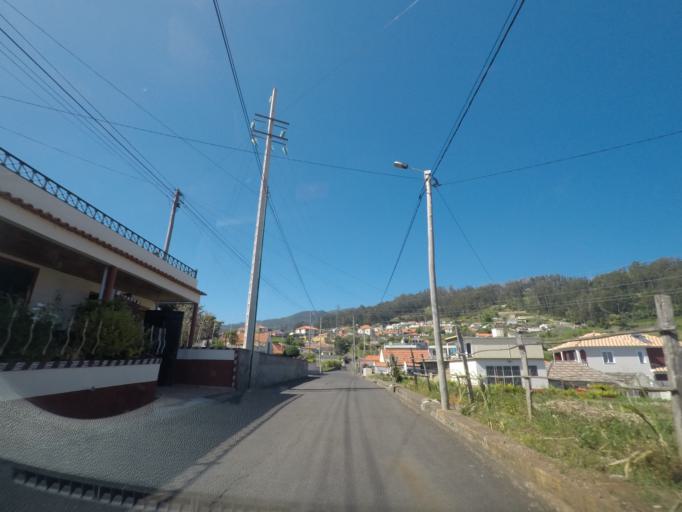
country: PT
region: Madeira
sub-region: Calheta
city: Arco da Calheta
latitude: 32.7062
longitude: -17.1165
